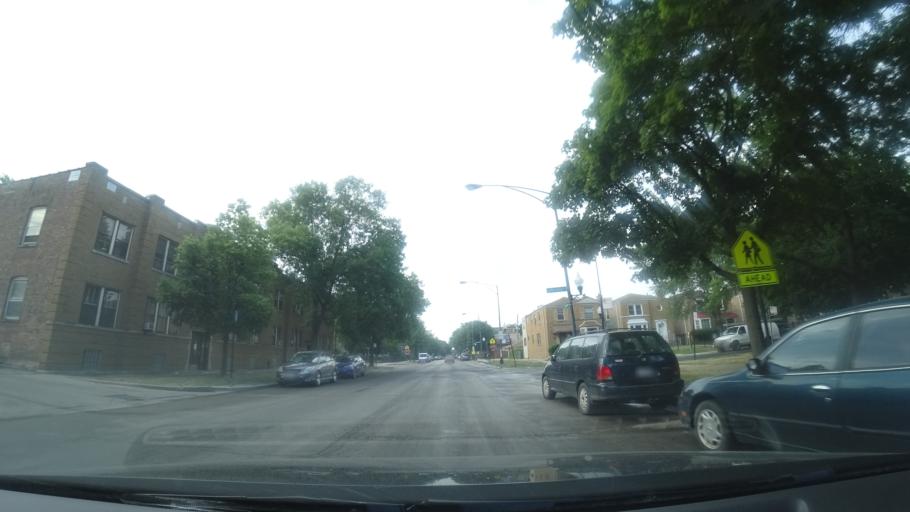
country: US
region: Illinois
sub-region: Cook County
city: Oak Park
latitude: 41.9287
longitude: -87.7367
